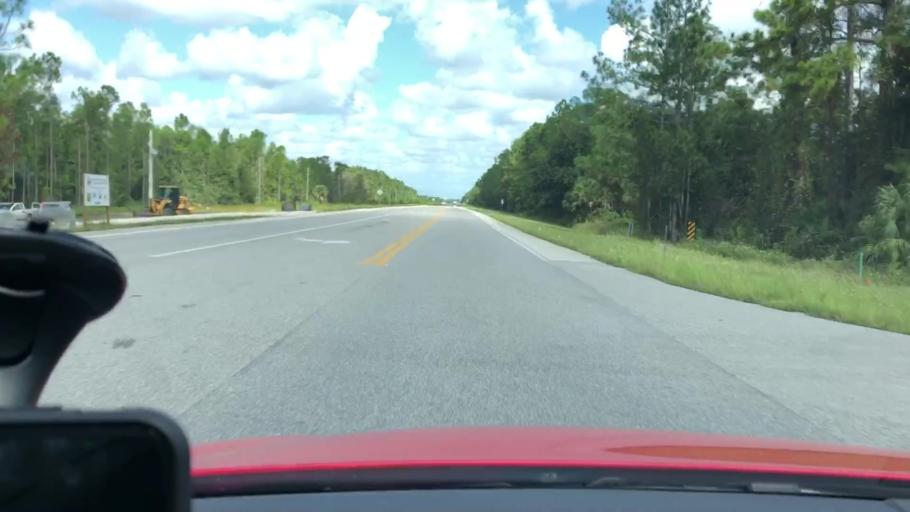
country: US
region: Florida
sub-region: Volusia County
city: Daytona Beach
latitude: 29.1790
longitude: -81.1197
